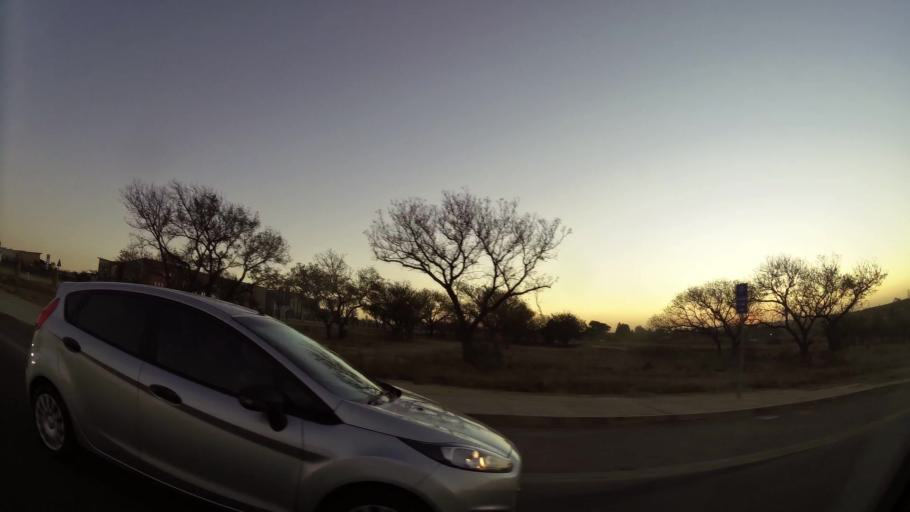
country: ZA
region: Gauteng
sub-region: City of Johannesburg Metropolitan Municipality
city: Diepsloot
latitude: -25.9618
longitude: 28.0244
